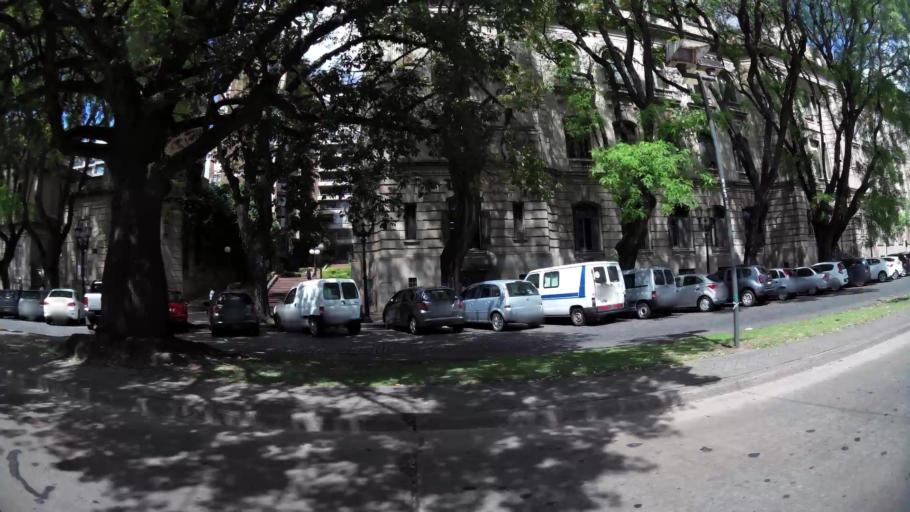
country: AR
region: Santa Fe
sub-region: Departamento de Rosario
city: Rosario
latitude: -32.9440
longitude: -60.6336
